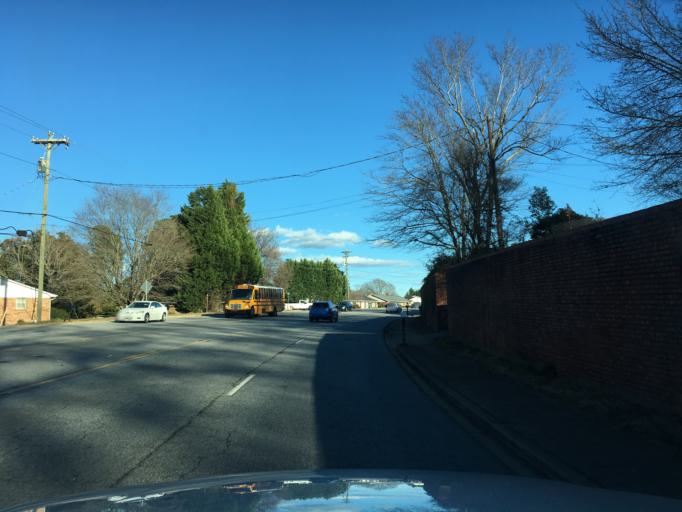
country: US
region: South Carolina
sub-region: Greenville County
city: Wade Hampton
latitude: 34.8724
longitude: -82.3354
